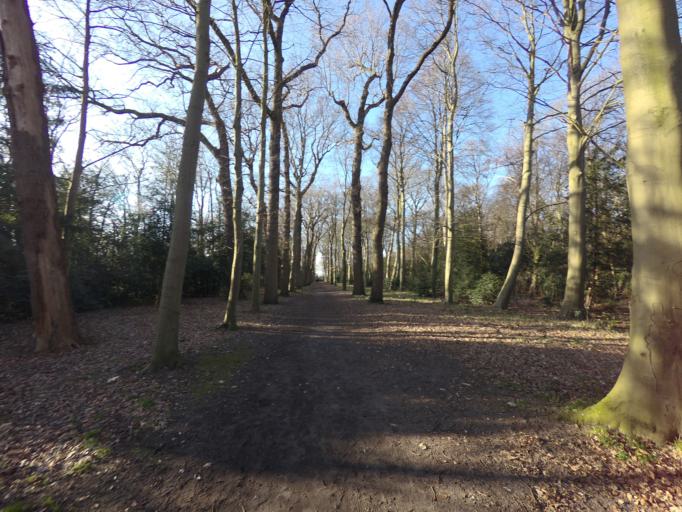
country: NL
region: South Holland
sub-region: Gemeente Teylingen
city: Sassenheim
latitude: 52.2018
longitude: 4.5099
